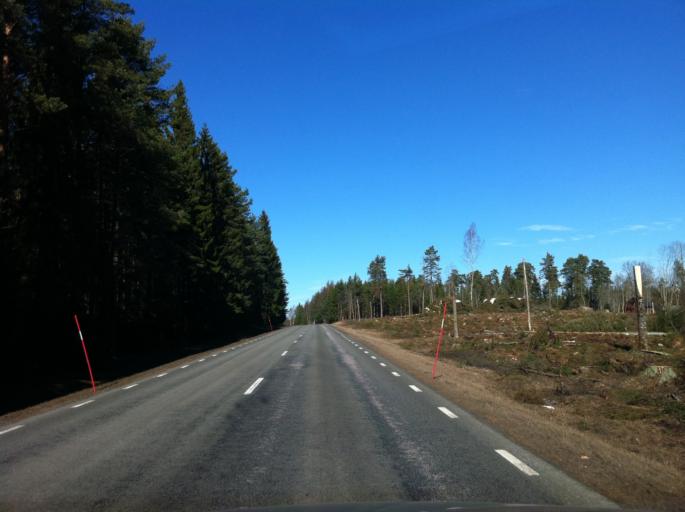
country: SE
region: Vaestra Goetaland
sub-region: Toreboda Kommun
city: Toereboda
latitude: 58.7746
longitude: 14.0905
